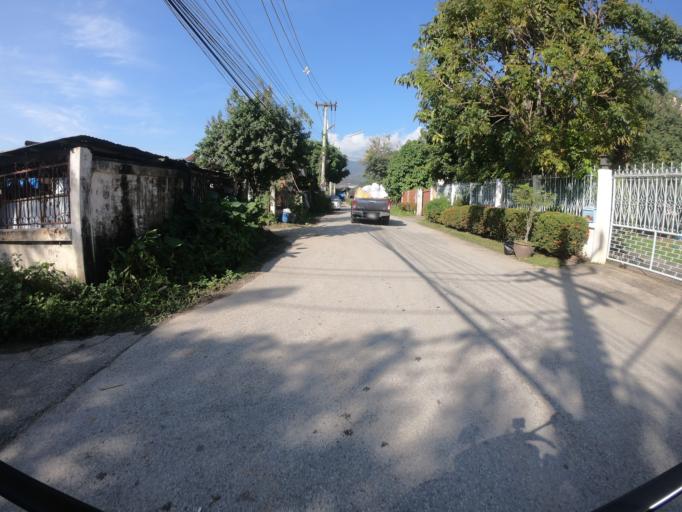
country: TH
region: Chiang Mai
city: Chiang Mai
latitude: 18.7881
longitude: 98.9655
